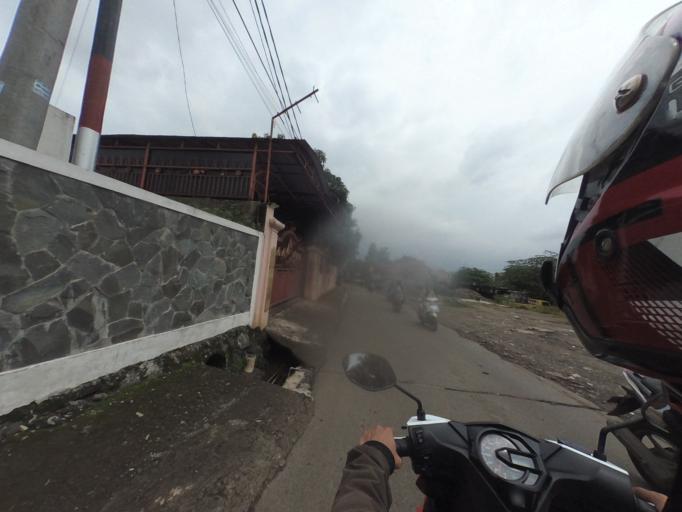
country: ID
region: West Java
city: Bogor
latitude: -6.6067
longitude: 106.7584
